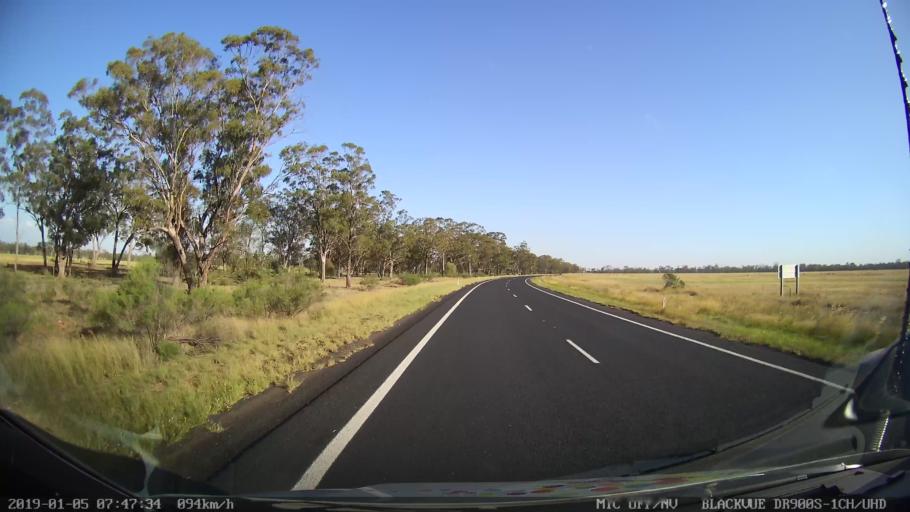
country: AU
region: New South Wales
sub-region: Gilgandra
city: Gilgandra
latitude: -31.8287
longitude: 148.6384
